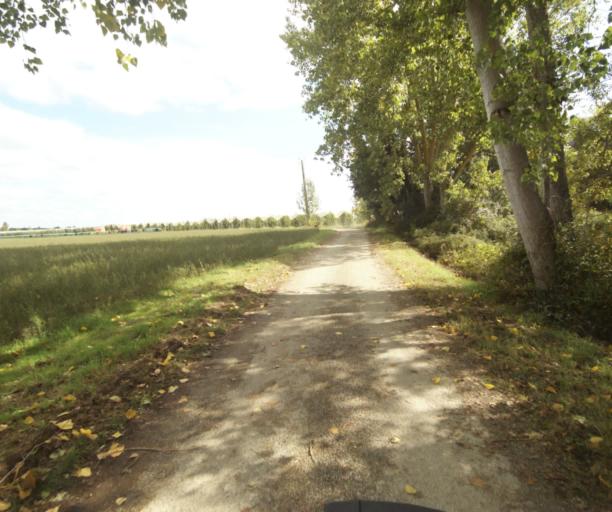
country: FR
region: Midi-Pyrenees
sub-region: Departement du Tarn-et-Garonne
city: Montech
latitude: 43.9496
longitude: 1.1927
